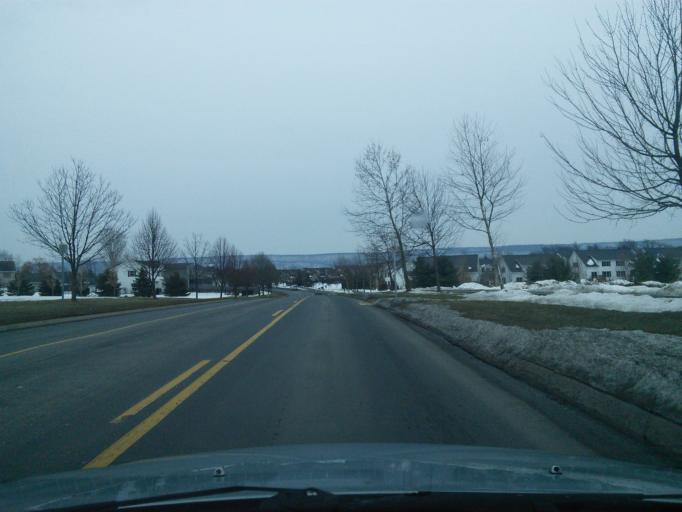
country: US
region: Pennsylvania
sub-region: Centre County
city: State College
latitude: 40.7738
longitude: -77.8736
